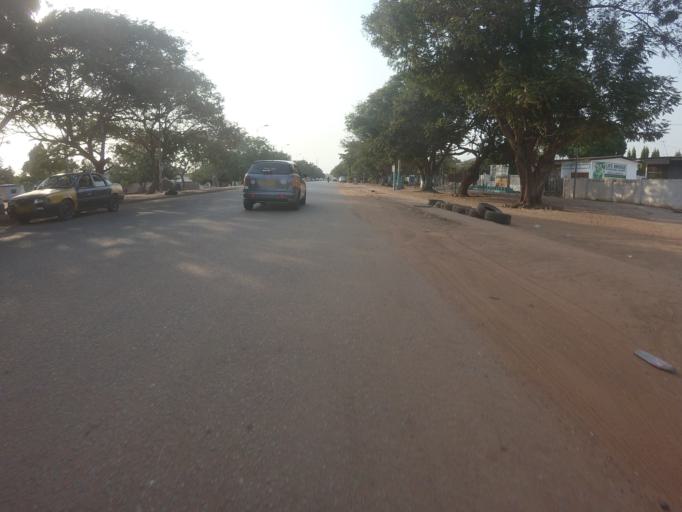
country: GH
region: Greater Accra
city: Nungua
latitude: 5.6224
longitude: -0.0573
